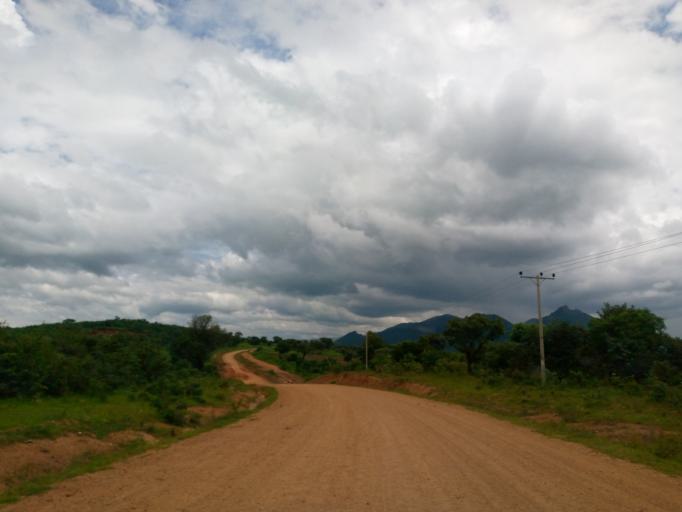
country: ET
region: Oromiya
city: Mendi
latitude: 10.1976
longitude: 35.0914
